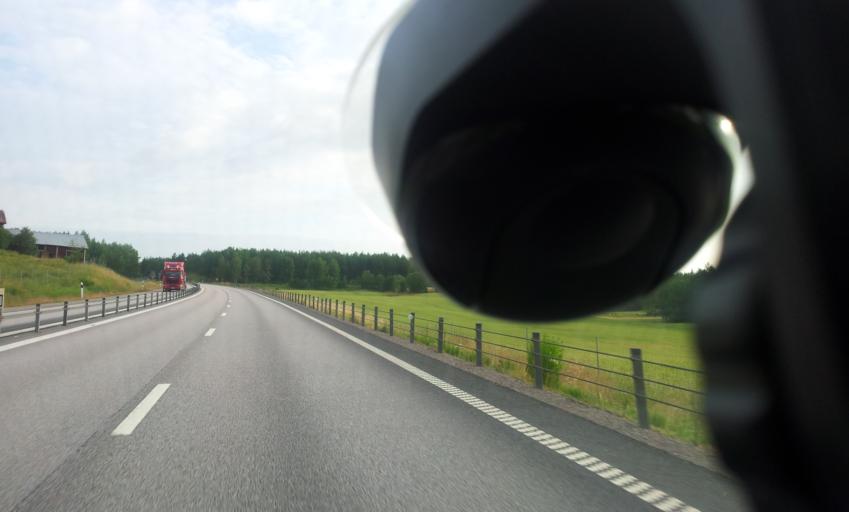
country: SE
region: OEstergoetland
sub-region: Valdemarsviks Kommun
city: Valdemarsvik
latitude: 58.2273
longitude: 16.5529
